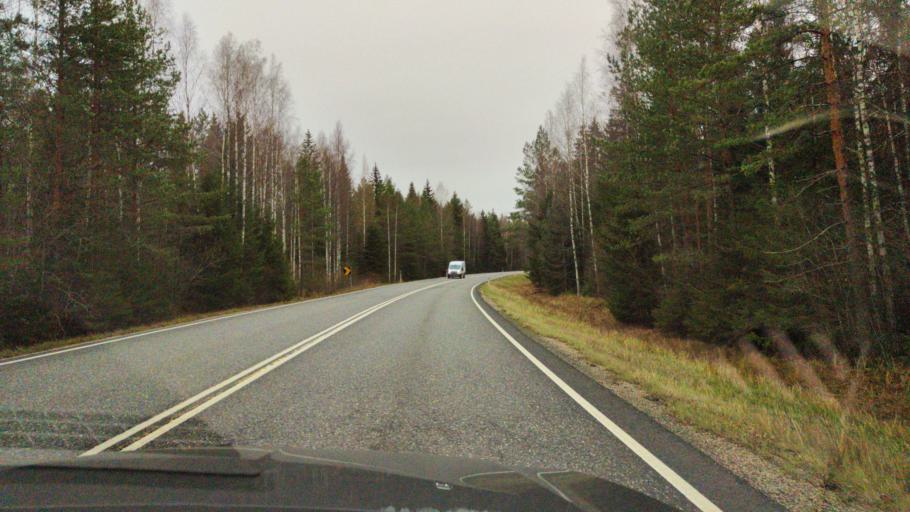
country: FI
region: Varsinais-Suomi
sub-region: Loimaa
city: Ylaene
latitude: 60.7392
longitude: 22.4268
